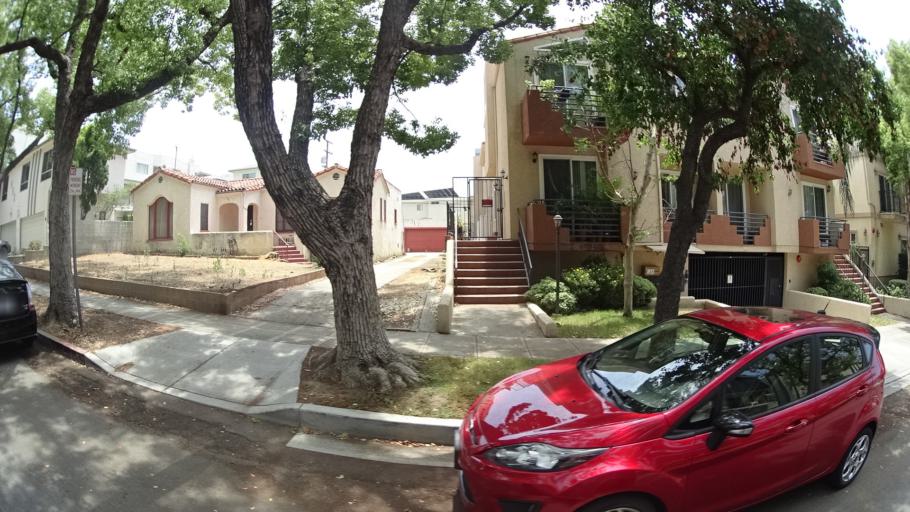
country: US
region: California
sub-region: Los Angeles County
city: Burbank
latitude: 34.1877
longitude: -118.3085
